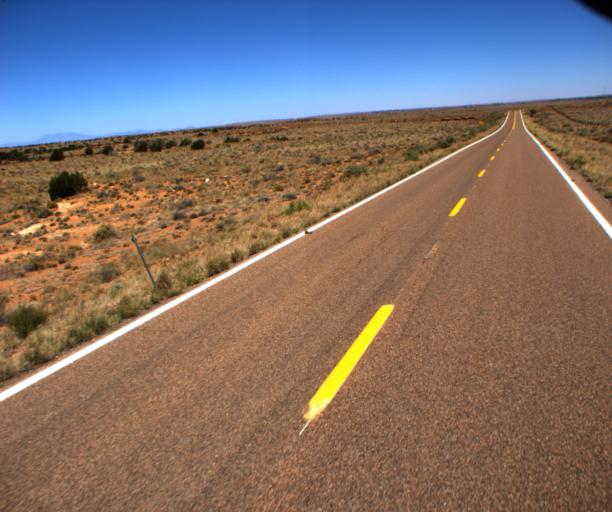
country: US
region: Arizona
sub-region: Navajo County
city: Winslow
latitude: 34.9318
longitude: -110.6389
